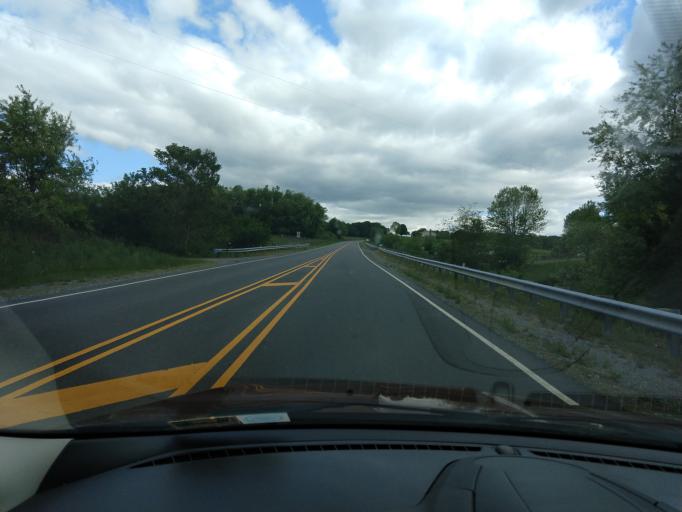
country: US
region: Virginia
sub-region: Wythe County
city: Wytheville
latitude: 36.8744
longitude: -80.9831
